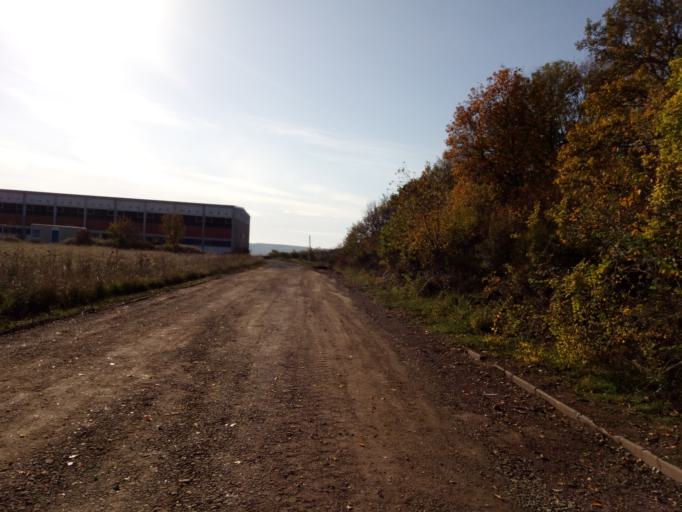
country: DE
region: Rheinland-Pfalz
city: Nussbaum
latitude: 49.8076
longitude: 7.6321
